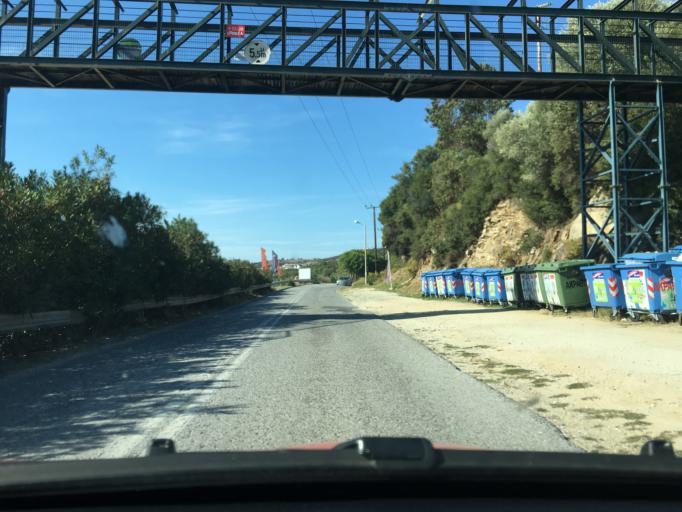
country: GR
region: Central Macedonia
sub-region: Nomos Chalkidikis
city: Ouranoupolis
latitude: 40.3453
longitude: 23.9651
